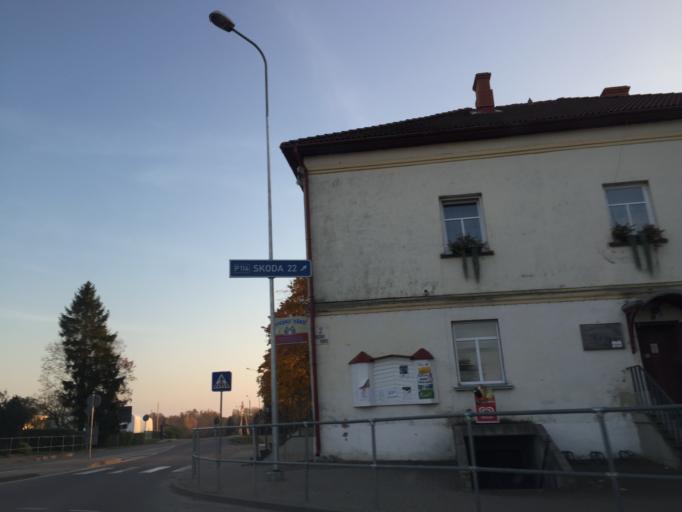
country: LV
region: Priekule
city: Priekule
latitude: 56.4388
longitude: 21.5831
